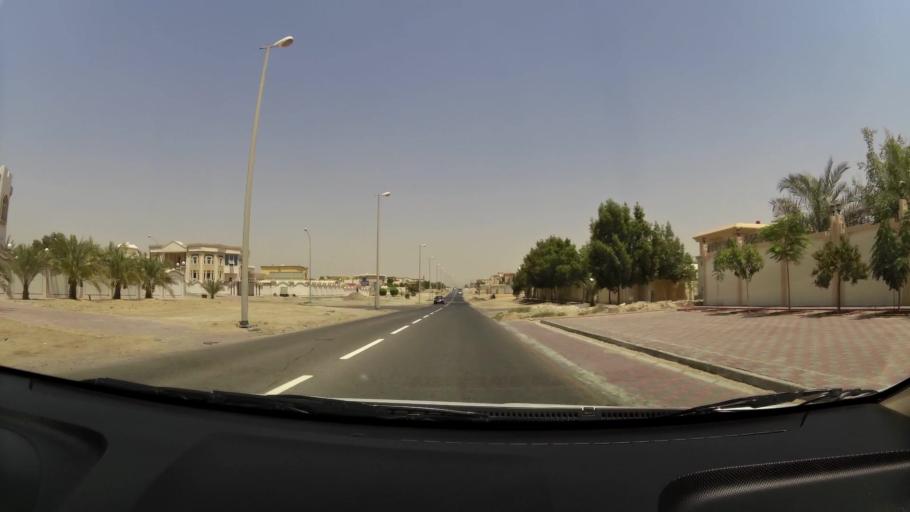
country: AE
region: Ajman
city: Ajman
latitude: 25.4215
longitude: 55.5078
